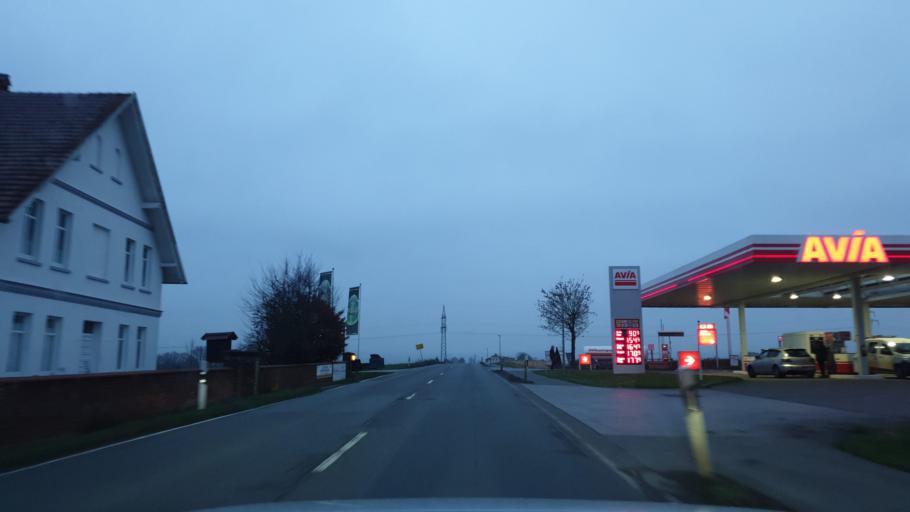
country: DE
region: North Rhine-Westphalia
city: Bad Oeynhausen
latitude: 52.2470
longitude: 8.7837
